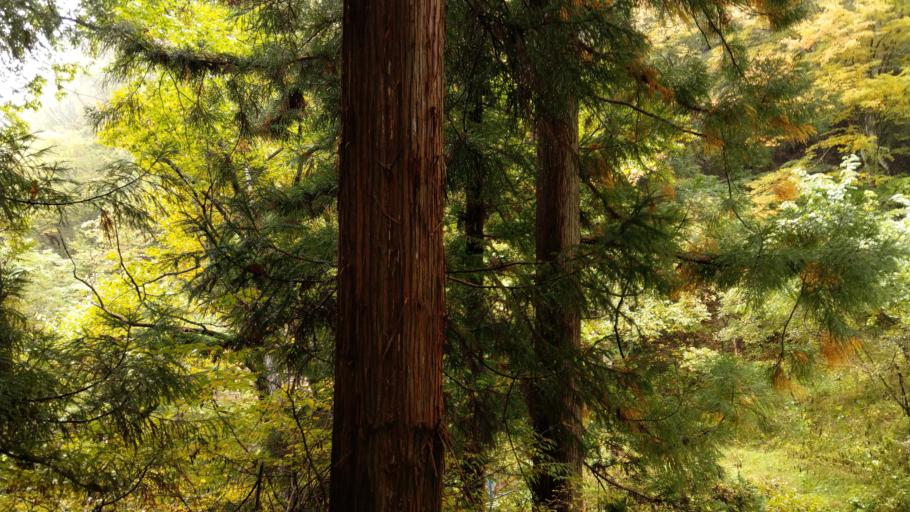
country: JP
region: Nagano
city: Komoro
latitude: 36.3658
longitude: 138.4414
